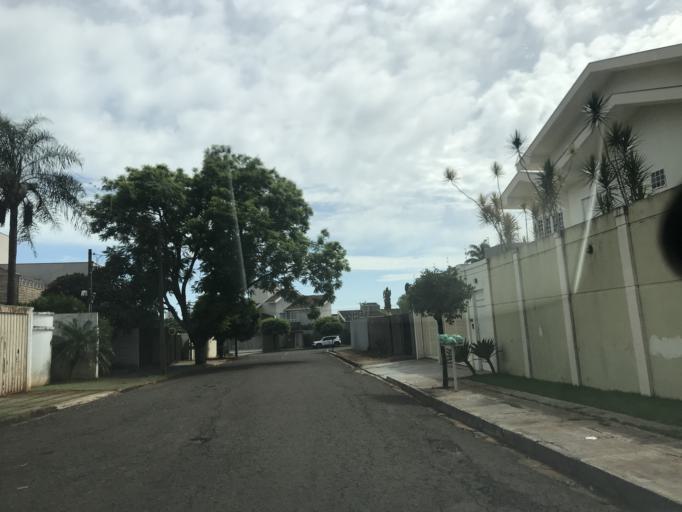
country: BR
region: Parana
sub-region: Londrina
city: Londrina
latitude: -23.3467
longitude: -51.1613
